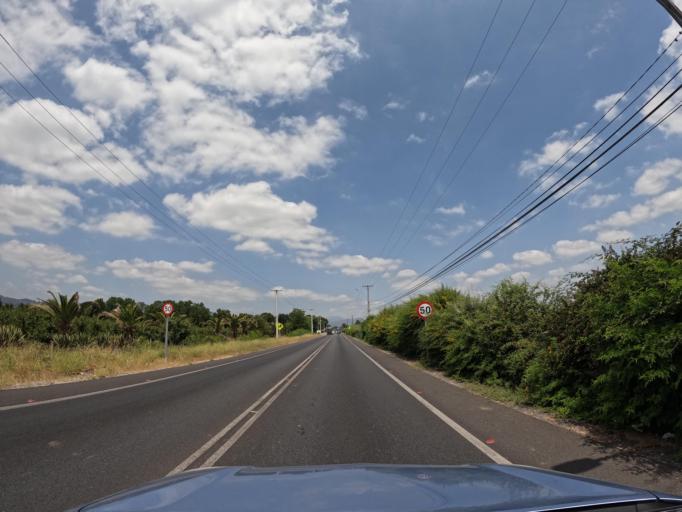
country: CL
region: Maule
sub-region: Provincia de Curico
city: Curico
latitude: -35.0271
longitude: -71.1963
